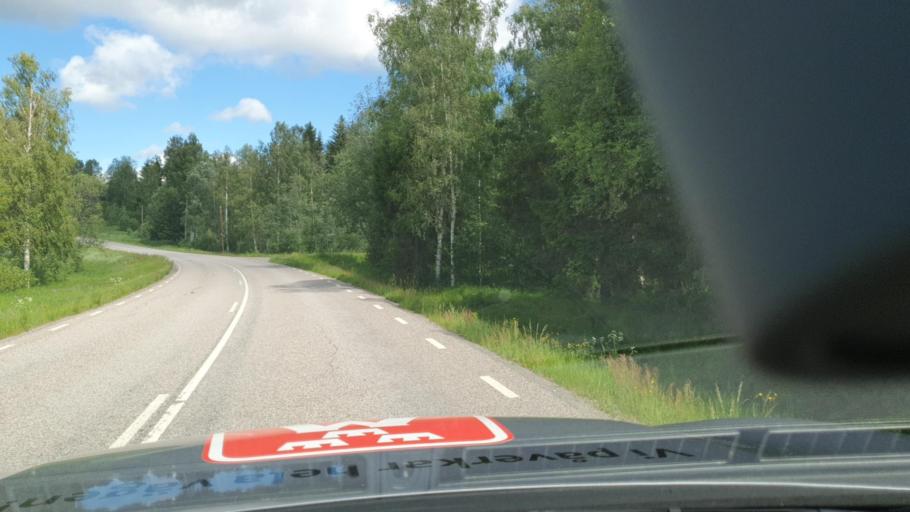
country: SE
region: Vaesternorrland
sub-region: OErnskoeldsviks Kommun
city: Bjasta
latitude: 63.2820
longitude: 18.2961
